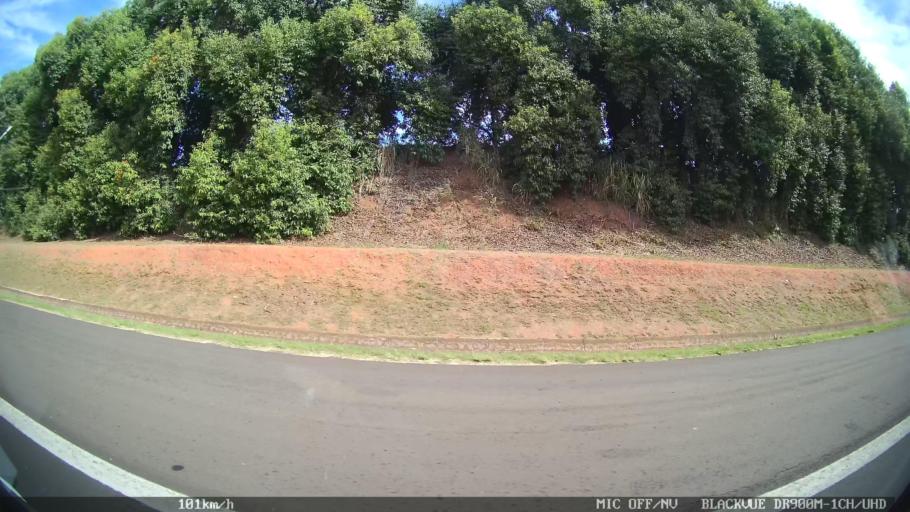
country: BR
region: Sao Paulo
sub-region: Matao
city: Matao
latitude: -21.6296
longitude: -48.4053
